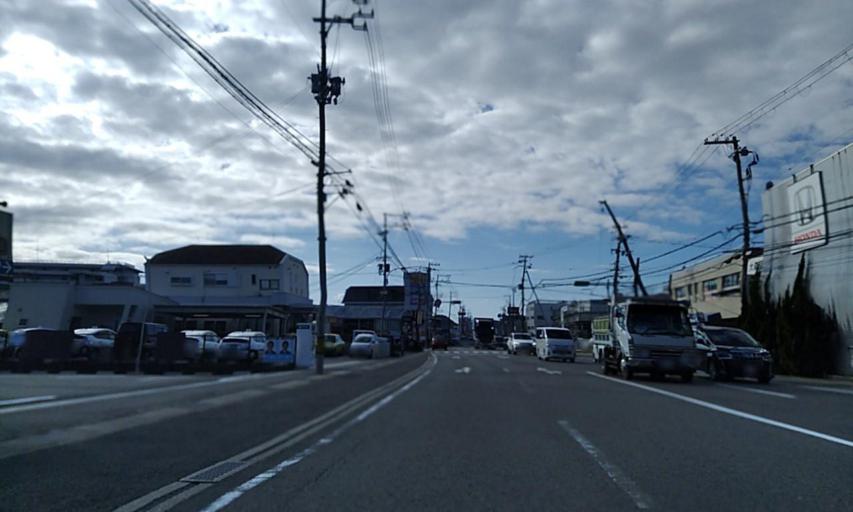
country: JP
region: Wakayama
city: Minato
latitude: 34.2179
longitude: 135.1595
